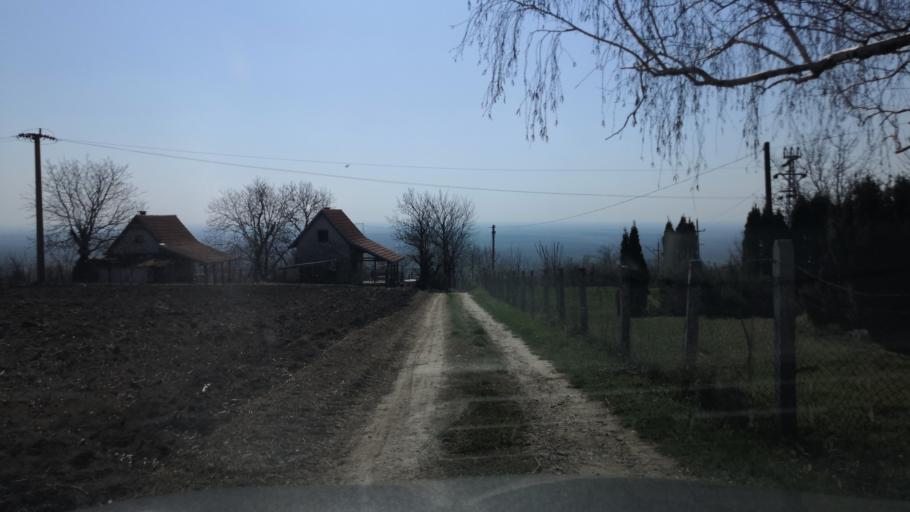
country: RS
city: Krcedin
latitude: 45.1619
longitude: 20.1868
